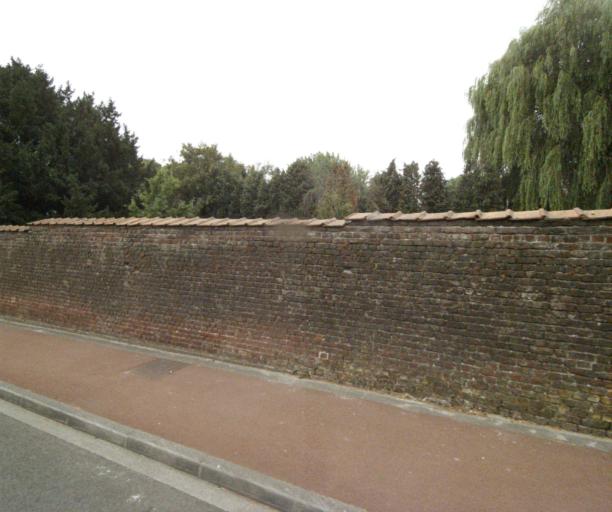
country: FR
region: Nord-Pas-de-Calais
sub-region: Departement du Nord
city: Mouvaux
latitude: 50.7052
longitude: 3.1308
